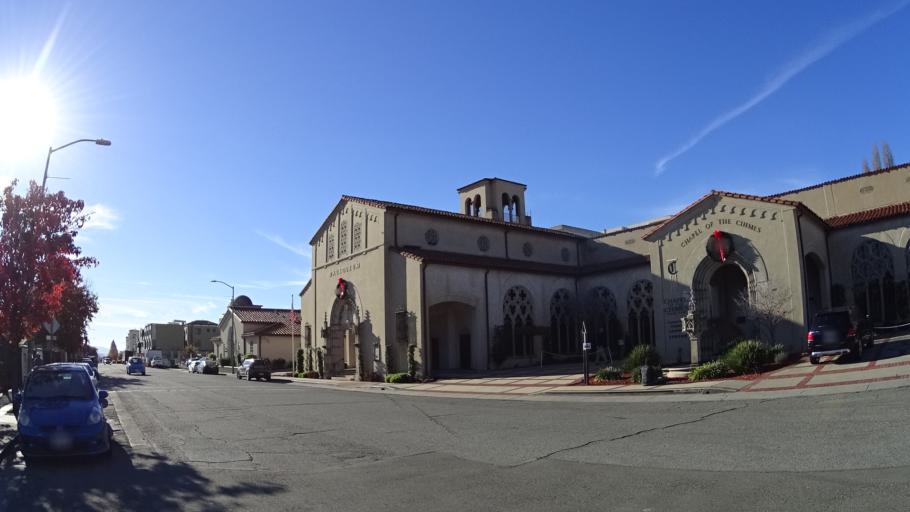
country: US
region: California
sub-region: Alameda County
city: Piedmont
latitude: 37.8316
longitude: -122.2455
